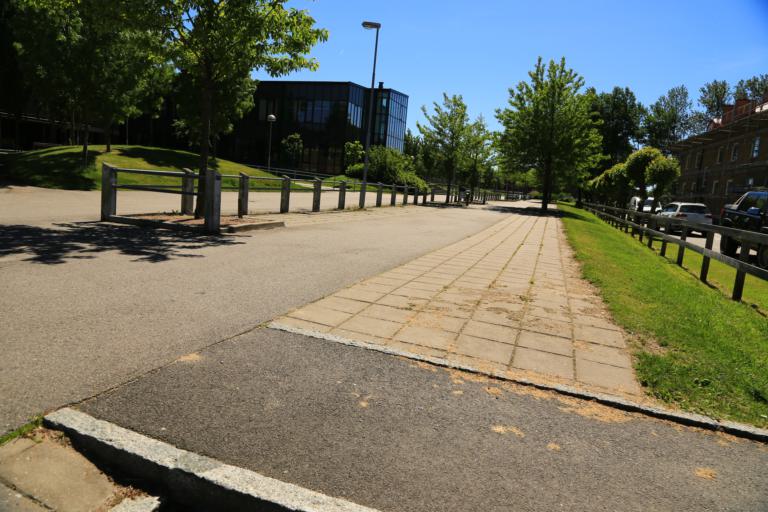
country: SE
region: Halland
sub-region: Varbergs Kommun
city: Varberg
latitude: 57.1064
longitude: 12.2703
